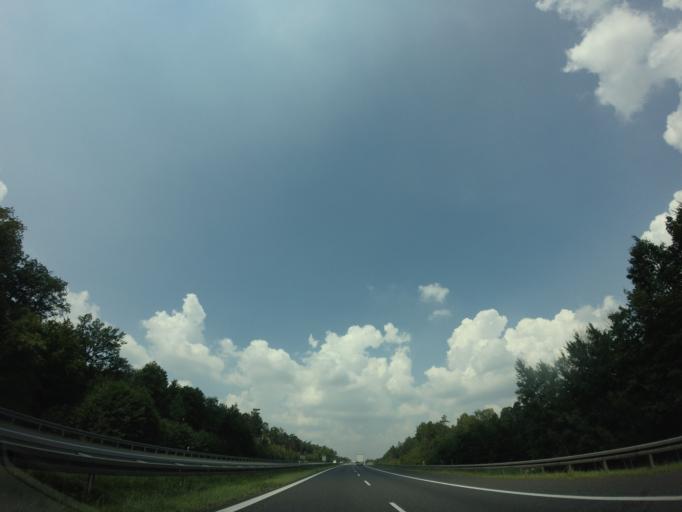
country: PL
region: Silesian Voivodeship
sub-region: Powiat gliwicki
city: Sosnicowice
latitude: 50.3540
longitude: 18.5237
